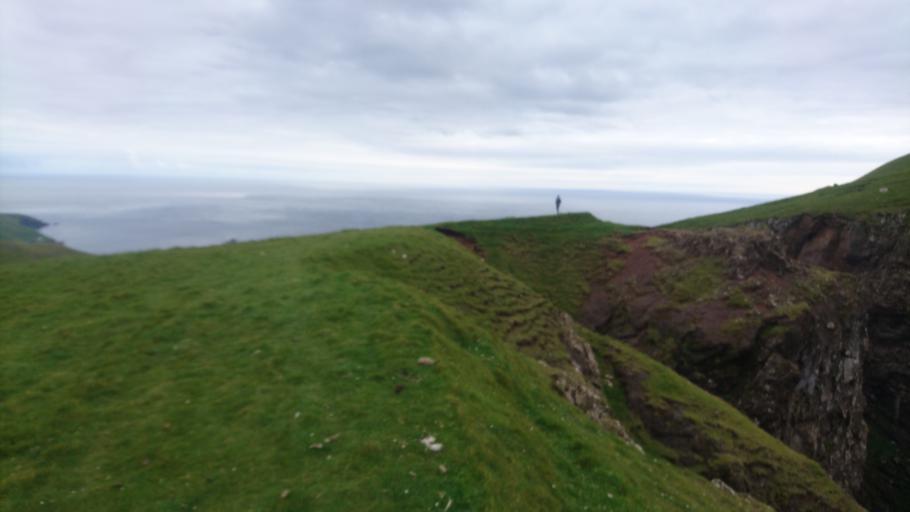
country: FO
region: Suduroy
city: Vagur
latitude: 61.4228
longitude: -6.7551
